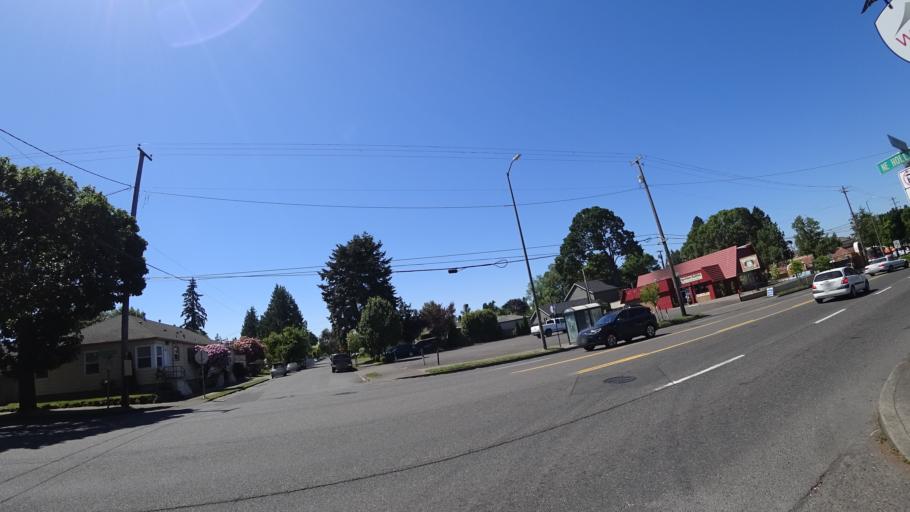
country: US
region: Oregon
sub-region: Multnomah County
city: Portland
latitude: 45.5759
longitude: -122.6612
